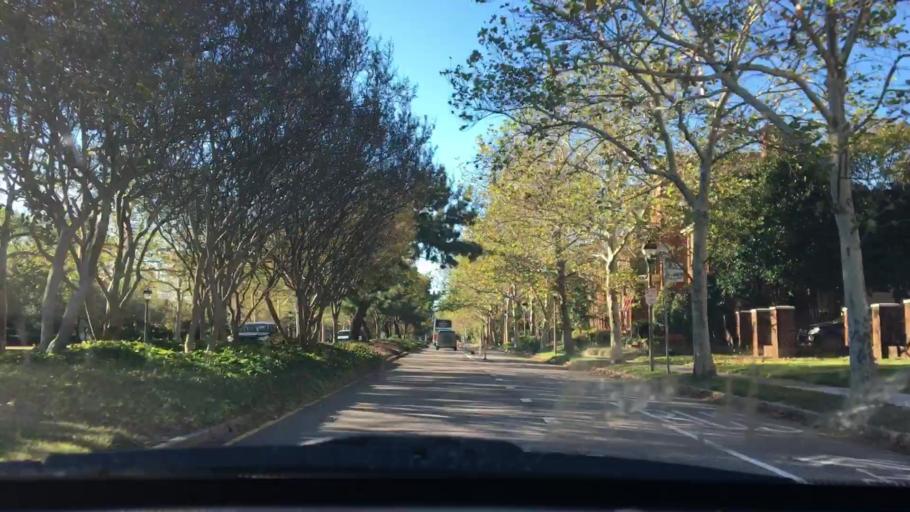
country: US
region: Virginia
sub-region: City of Norfolk
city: Norfolk
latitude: 36.8575
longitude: -76.2934
